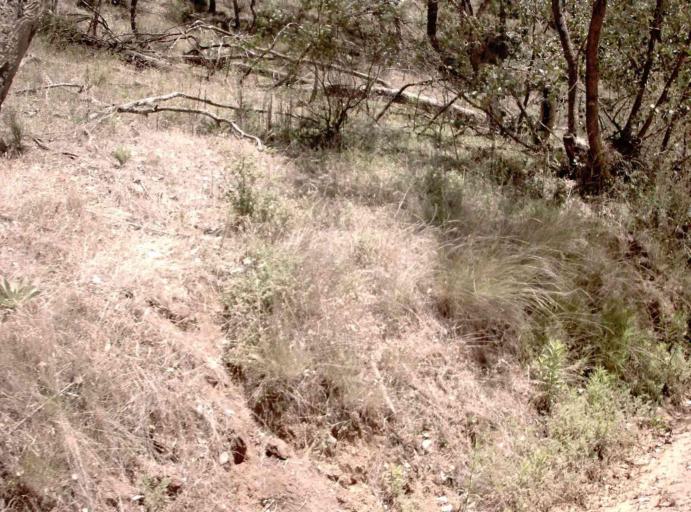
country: AU
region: New South Wales
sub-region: Snowy River
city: Jindabyne
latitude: -36.9167
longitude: 148.4213
